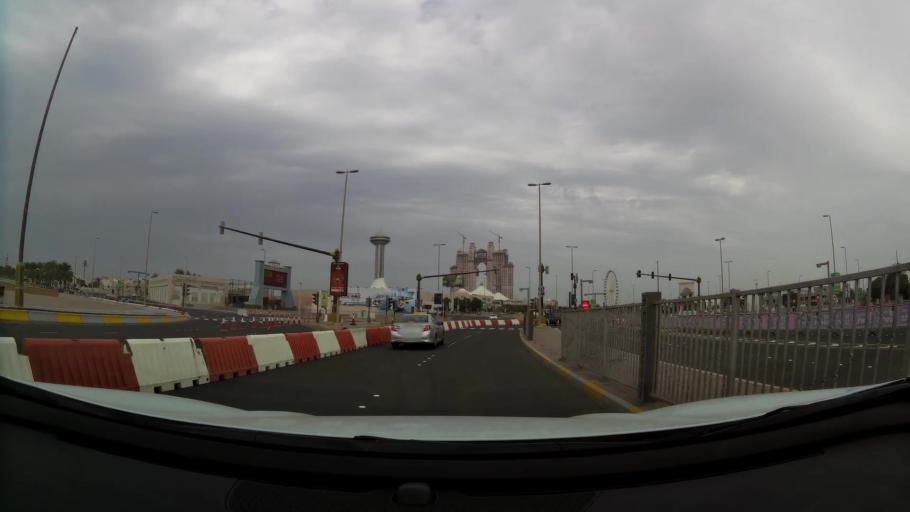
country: AE
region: Abu Dhabi
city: Abu Dhabi
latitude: 24.4710
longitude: 54.3222
